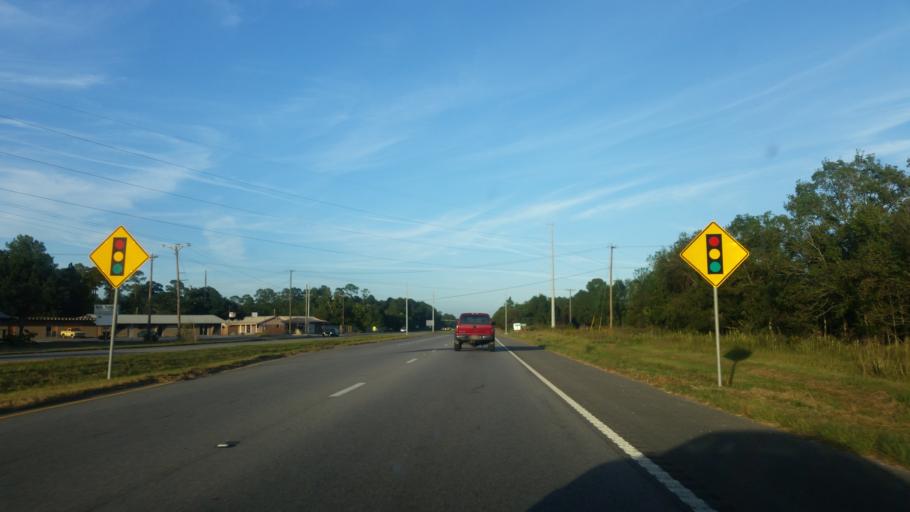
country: US
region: Mississippi
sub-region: Jackson County
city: Moss Point
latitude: 30.3978
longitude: -88.4957
